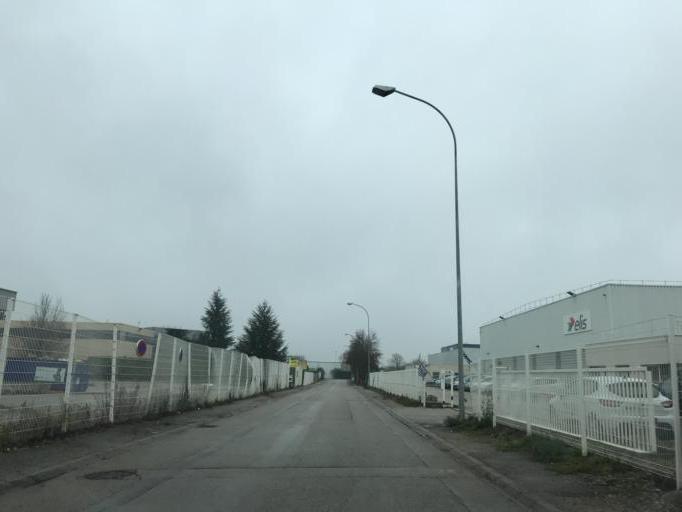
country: FR
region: Rhone-Alpes
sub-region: Departement du Rhone
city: Cailloux-sur-Fontaines
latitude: 45.8610
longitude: 4.9129
